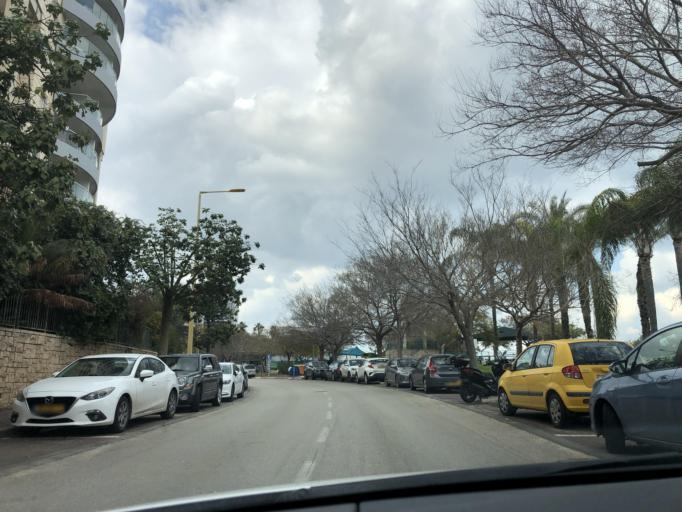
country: IL
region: Central District
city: Ganne Tiqwa
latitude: 32.0608
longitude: 34.8821
